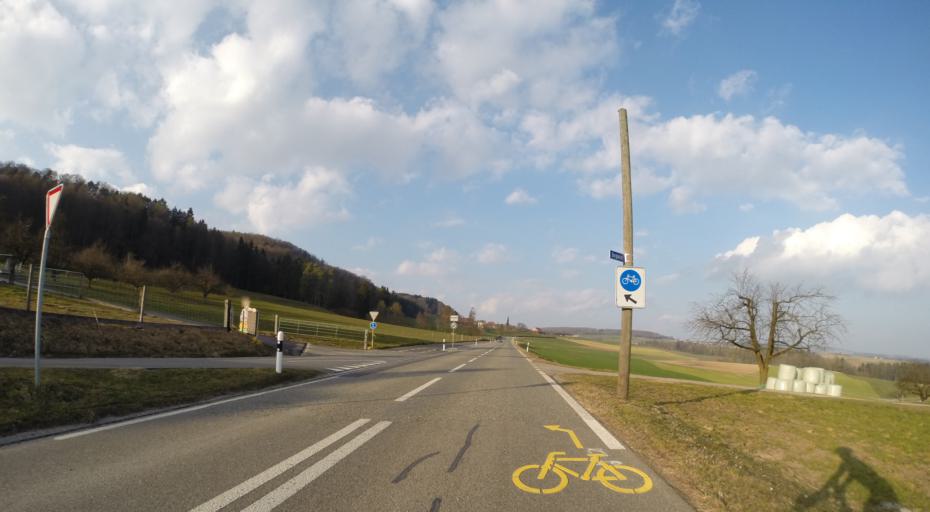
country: CH
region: Thurgau
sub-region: Frauenfeld District
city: Pfyn
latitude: 47.6098
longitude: 8.9153
